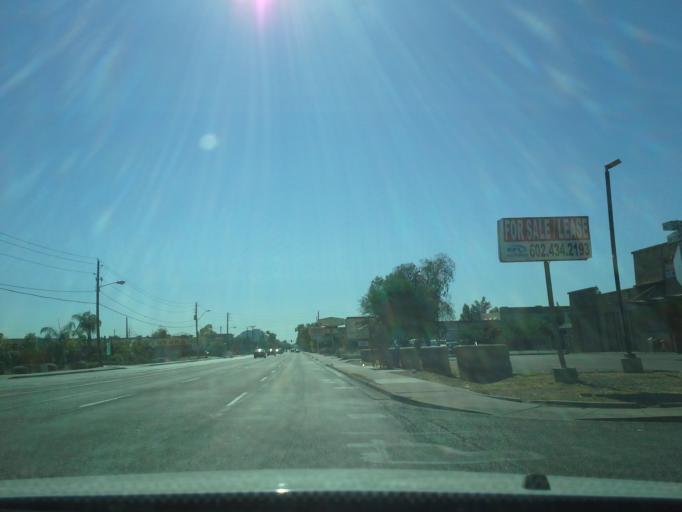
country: US
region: Arizona
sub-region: Maricopa County
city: Phoenix
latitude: 33.4657
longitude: -112.0082
